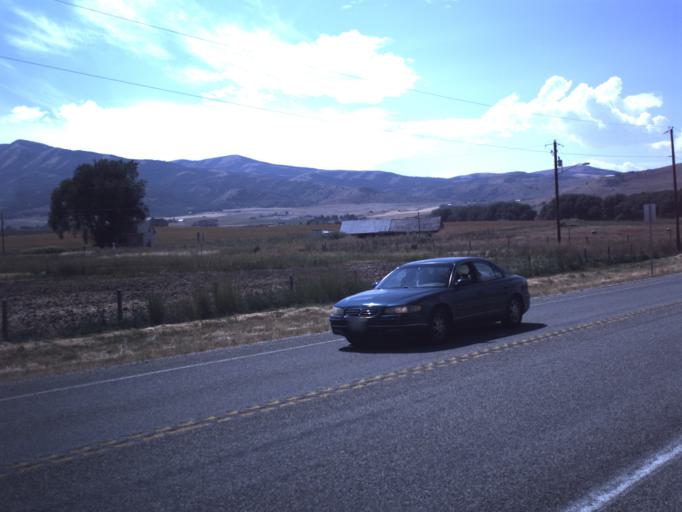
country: US
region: Utah
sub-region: Cache County
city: Mendon
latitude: 41.7503
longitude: -111.9774
